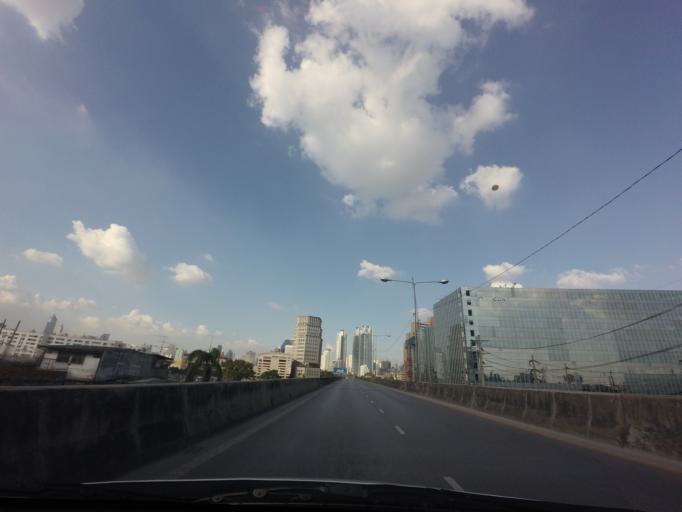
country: TH
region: Bangkok
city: Khlong Toei
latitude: 13.7195
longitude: 100.5588
